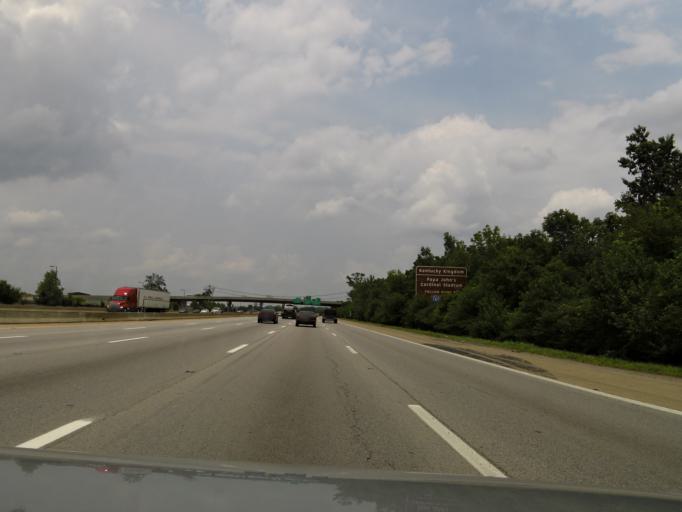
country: US
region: Kentucky
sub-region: Jefferson County
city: Audubon Park
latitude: 38.1666
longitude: -85.7206
